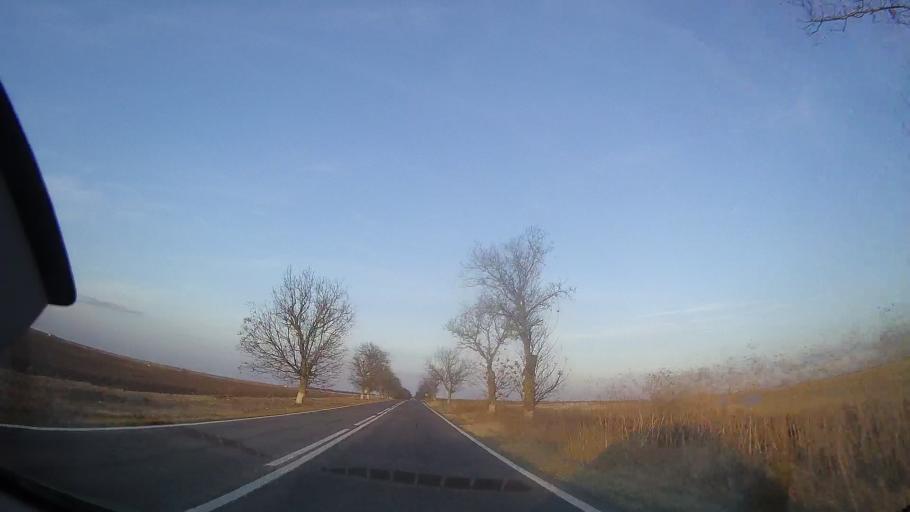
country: RO
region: Constanta
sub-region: Comuna Amzacea
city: Amzacea
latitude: 43.9858
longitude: 28.4201
